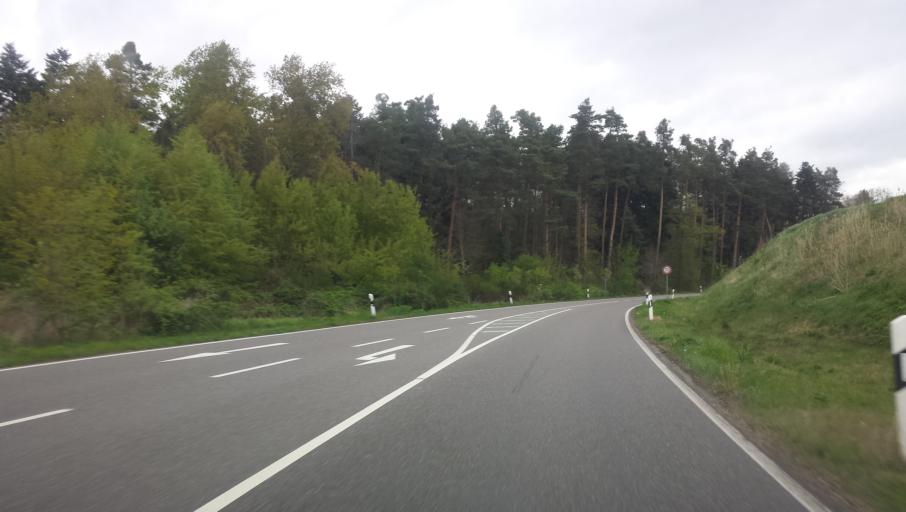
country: DE
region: Rheinland-Pfalz
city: Jockgrim
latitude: 49.0905
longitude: 8.2598
